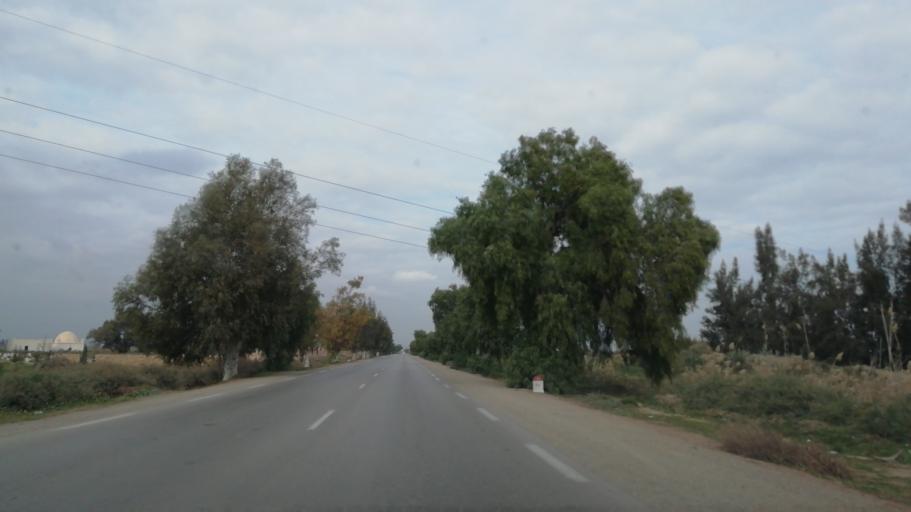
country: DZ
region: Mascara
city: Mascara
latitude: 35.6365
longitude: 0.0608
